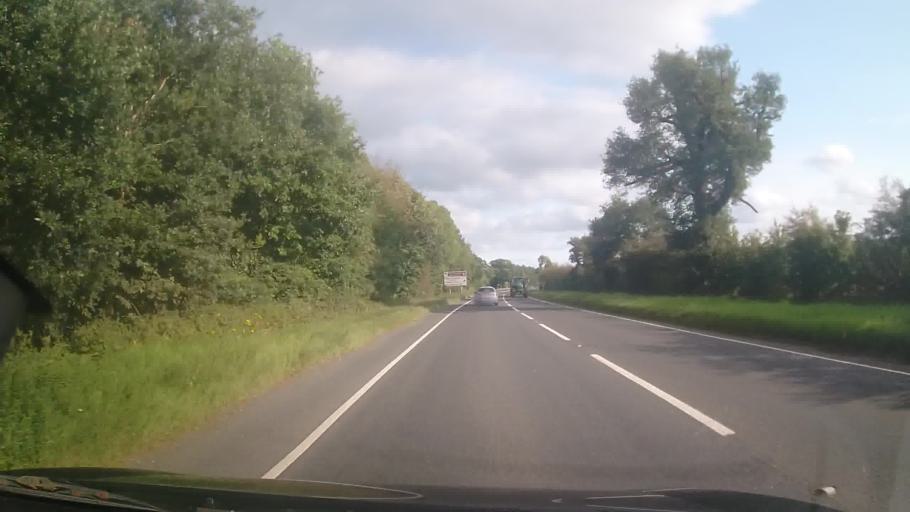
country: GB
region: England
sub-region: Shropshire
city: Bromfield
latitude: 52.3870
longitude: -2.7386
